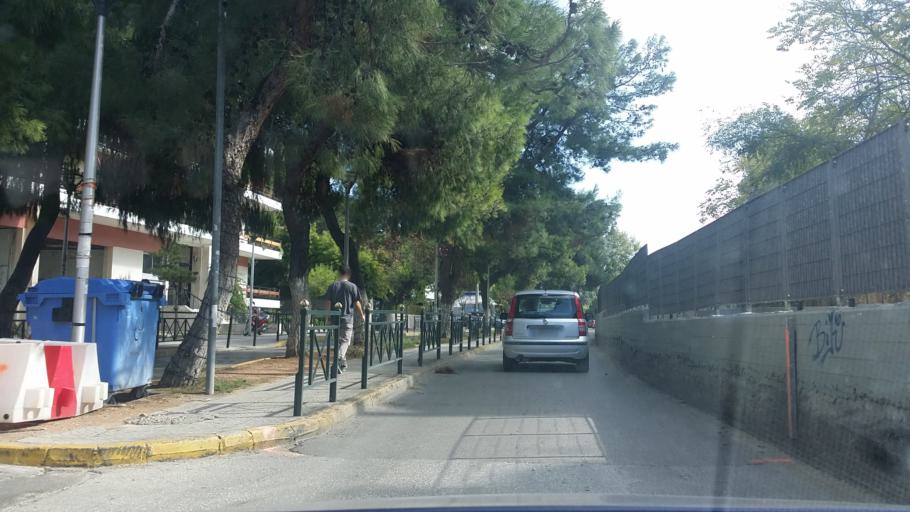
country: GR
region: Attica
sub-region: Nomarchia Athinas
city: Irakleio
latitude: 38.0470
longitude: 23.7645
